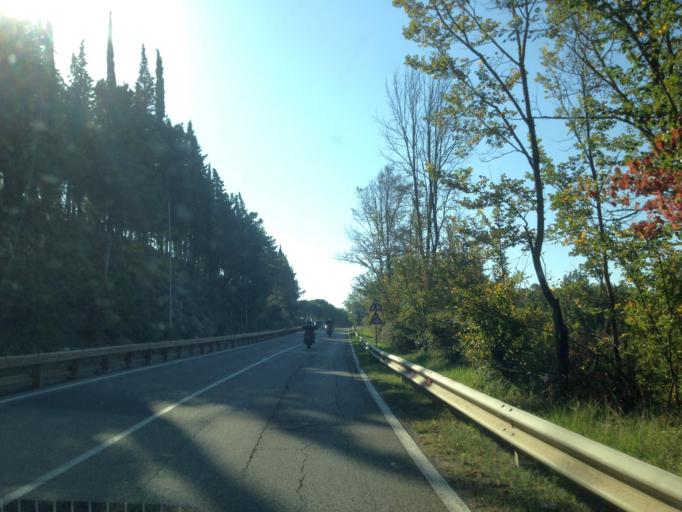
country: IT
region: Tuscany
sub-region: Provincia di Siena
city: Castellina in Chianti
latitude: 43.4585
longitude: 11.2919
